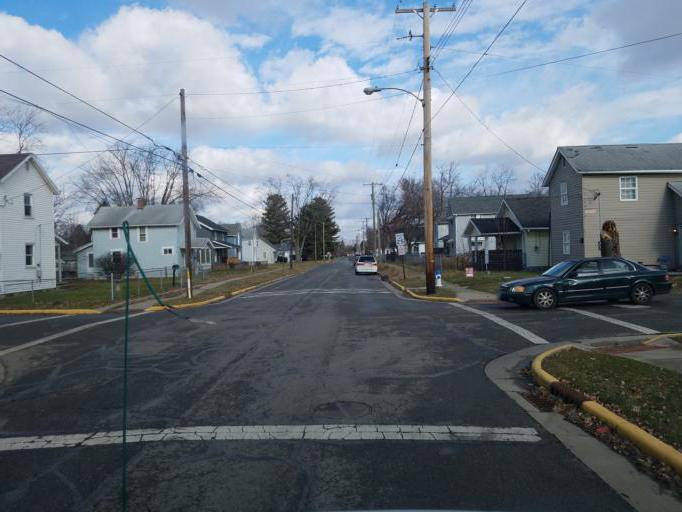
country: US
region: Ohio
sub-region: Marion County
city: Marion
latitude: 40.5828
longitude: -83.1539
